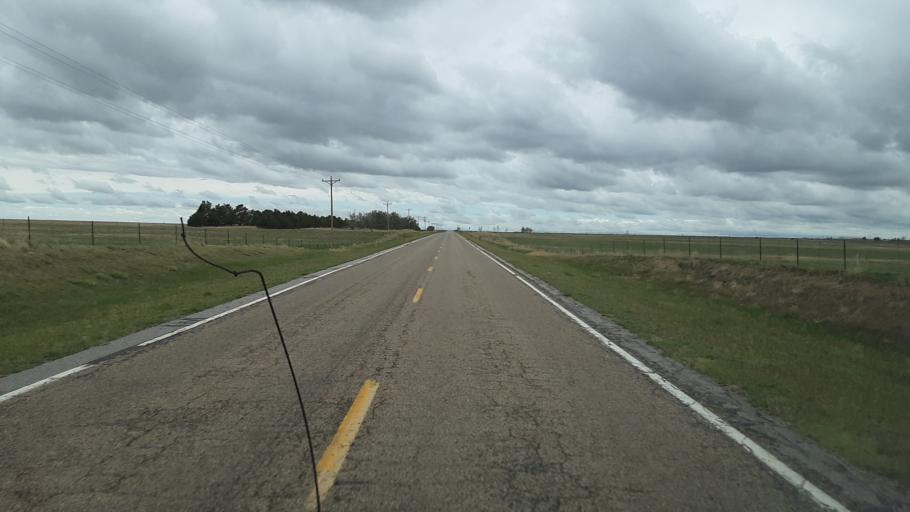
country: US
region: Colorado
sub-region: El Paso County
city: Ellicott
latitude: 38.8397
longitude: -103.9651
